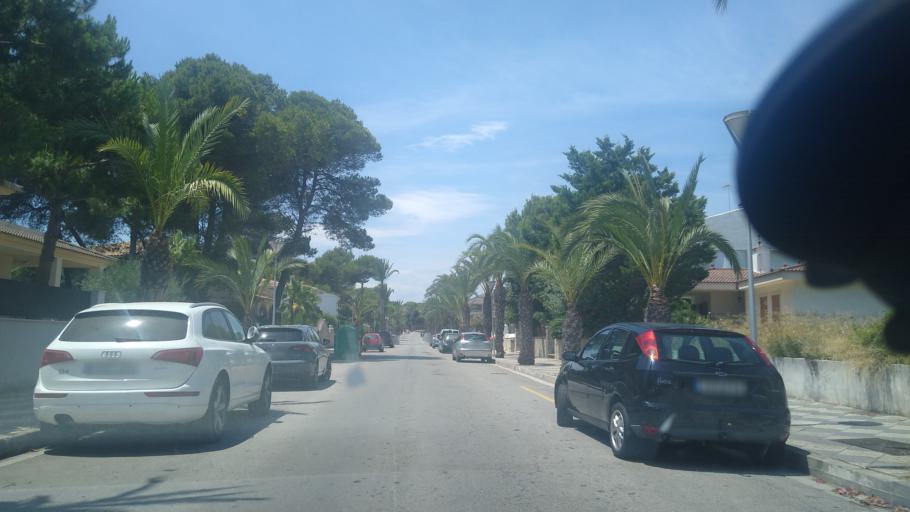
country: ES
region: Balearic Islands
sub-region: Illes Balears
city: Santa Margalida
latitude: 39.7595
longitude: 3.1634
